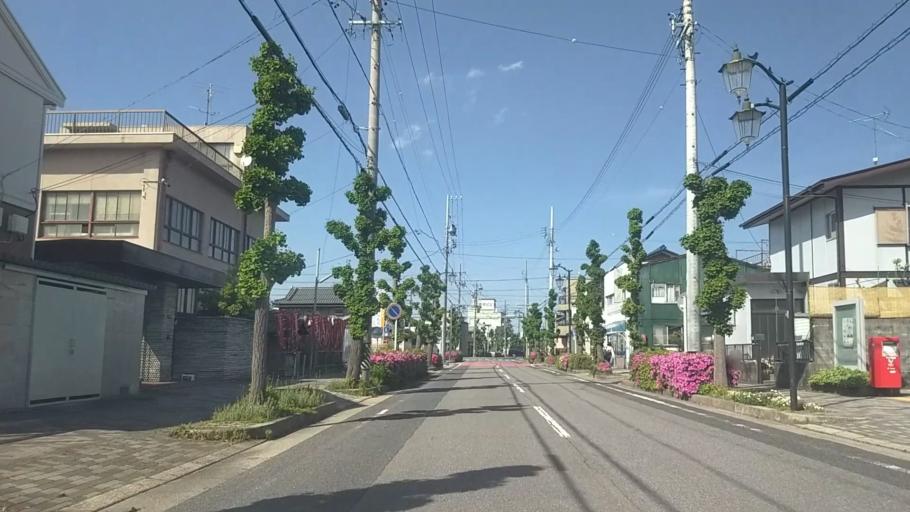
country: JP
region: Aichi
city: Anjo
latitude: 34.9611
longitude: 137.0878
